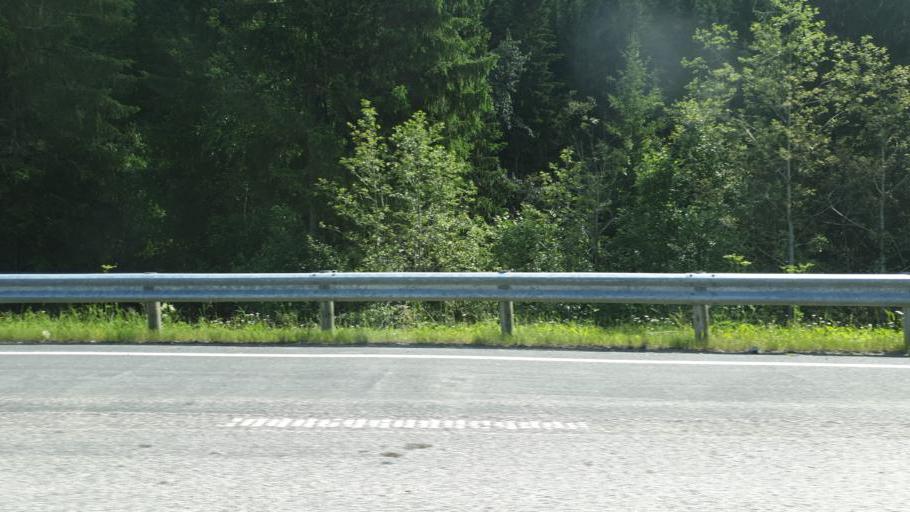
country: NO
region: Sor-Trondelag
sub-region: Midtre Gauldal
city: Storen
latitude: 62.9869
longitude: 10.2444
